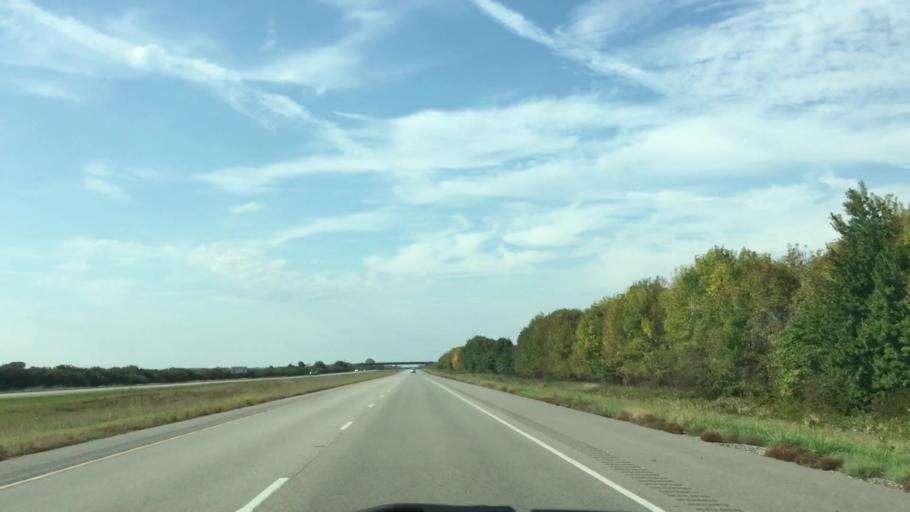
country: US
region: Illinois
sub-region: Whiteside County
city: Erie
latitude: 41.5898
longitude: -90.1991
